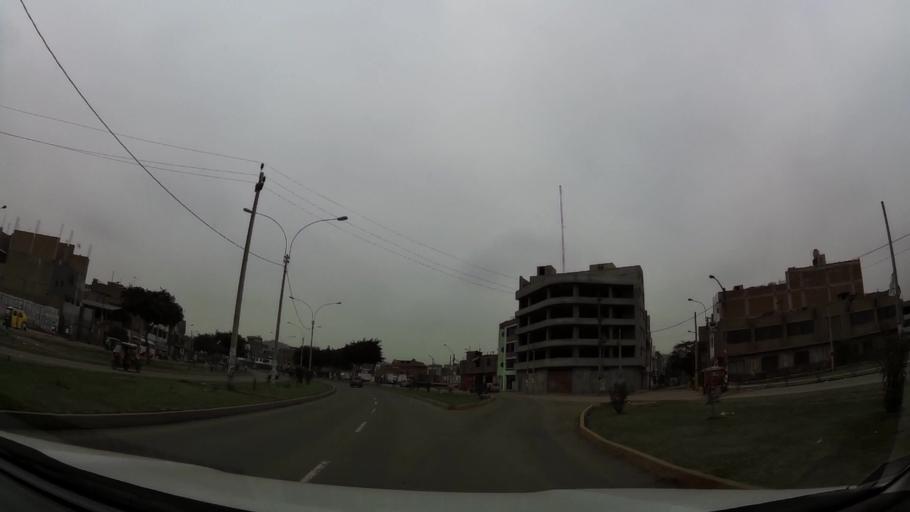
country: PE
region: Lima
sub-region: Lima
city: Vitarte
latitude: -12.0414
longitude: -76.9244
